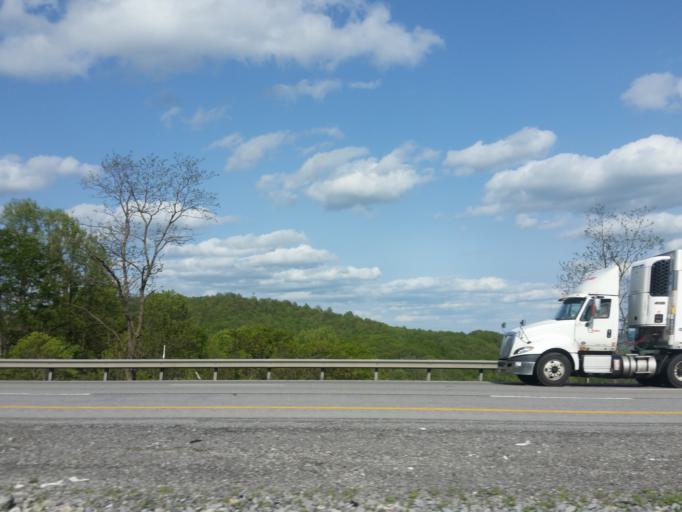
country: US
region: West Virginia
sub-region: Raleigh County
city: Shady Spring
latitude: 37.5579
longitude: -81.1133
